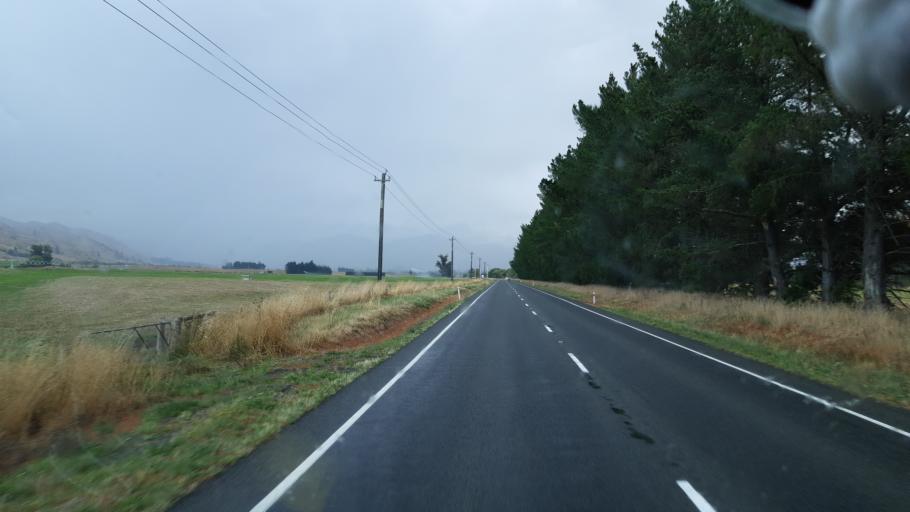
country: NZ
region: Canterbury
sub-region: Hurunui District
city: Amberley
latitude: -42.7089
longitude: 172.8455
